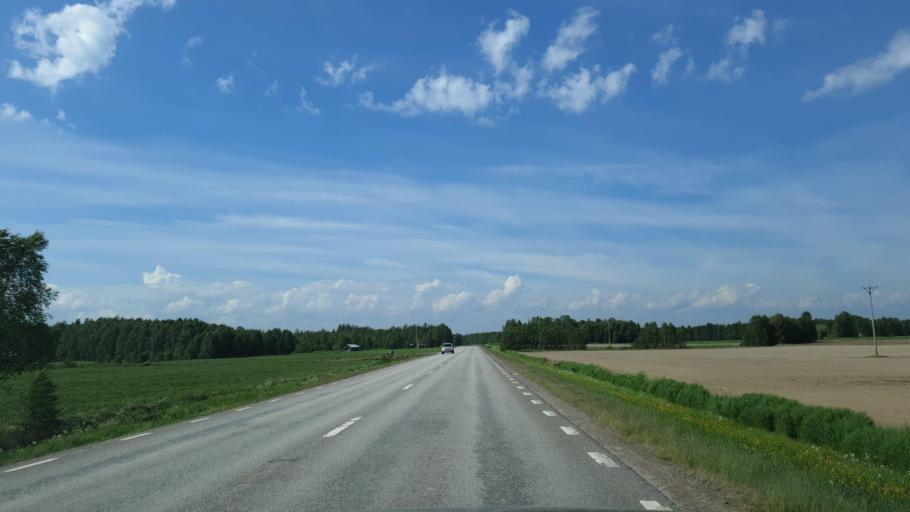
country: SE
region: Norrbotten
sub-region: Pitea Kommun
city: Rosvik
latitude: 65.5724
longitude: 21.7490
